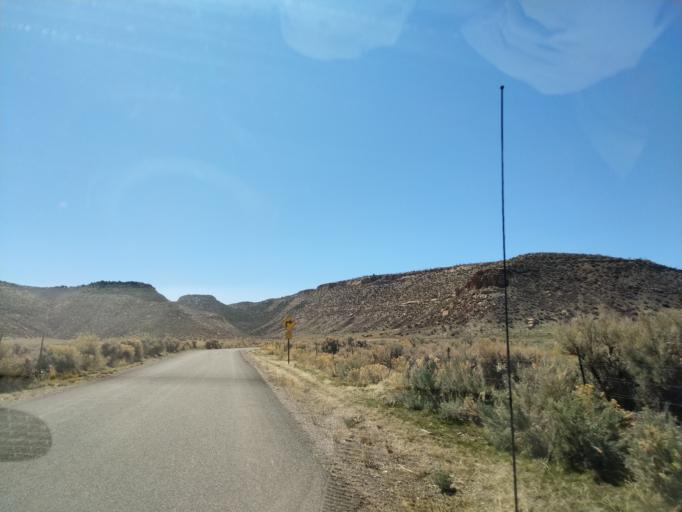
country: US
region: Colorado
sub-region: Mesa County
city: Loma
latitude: 38.9503
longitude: -109.0311
